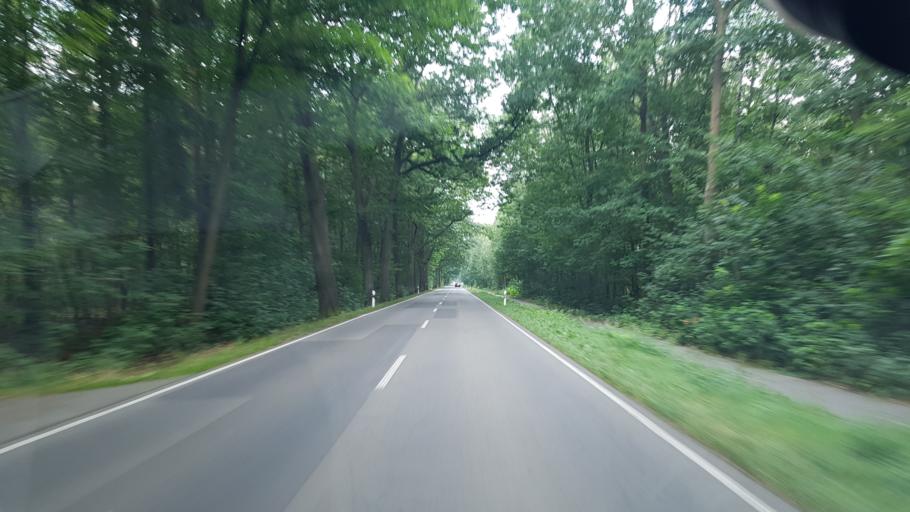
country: DE
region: Brandenburg
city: Tettau
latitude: 51.4440
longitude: 13.7345
